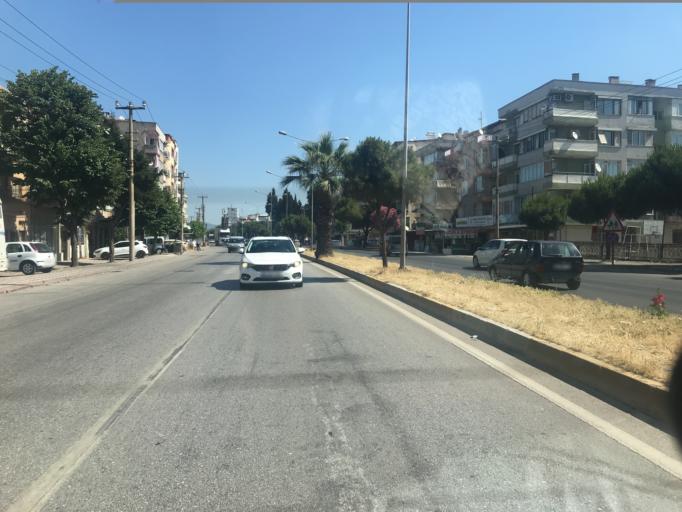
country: TR
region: Manisa
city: Akhisar
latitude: 38.9244
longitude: 27.8344
